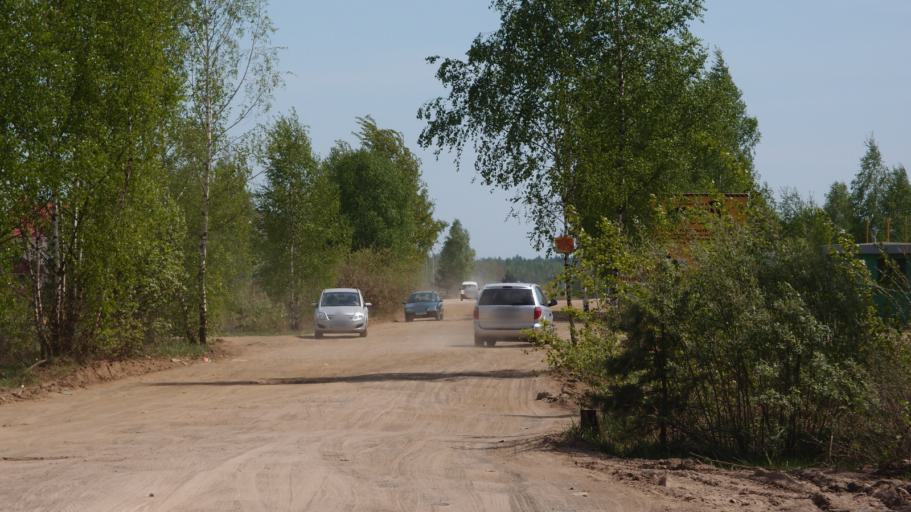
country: BY
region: Minsk
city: Kalodzishchy
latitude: 53.9191
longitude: 27.7527
